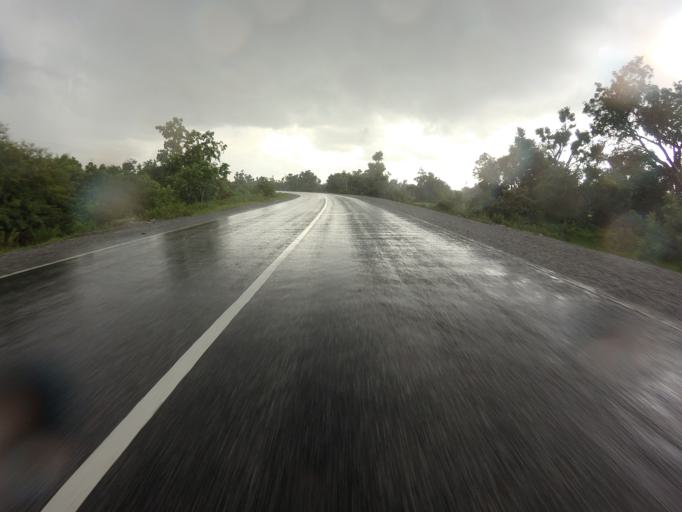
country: GH
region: Northern
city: Tamale
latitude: 9.1329
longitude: -1.5903
